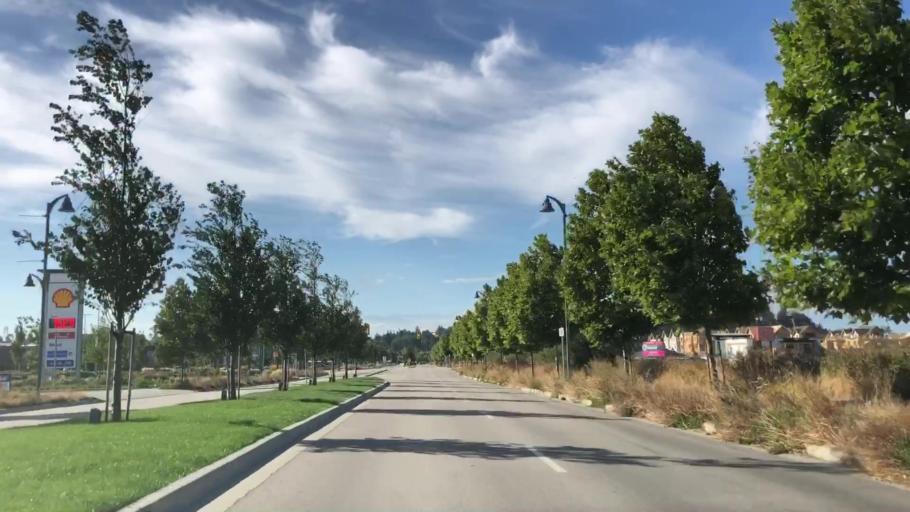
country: CA
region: British Columbia
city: Ladner
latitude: 49.0391
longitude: -123.0903
